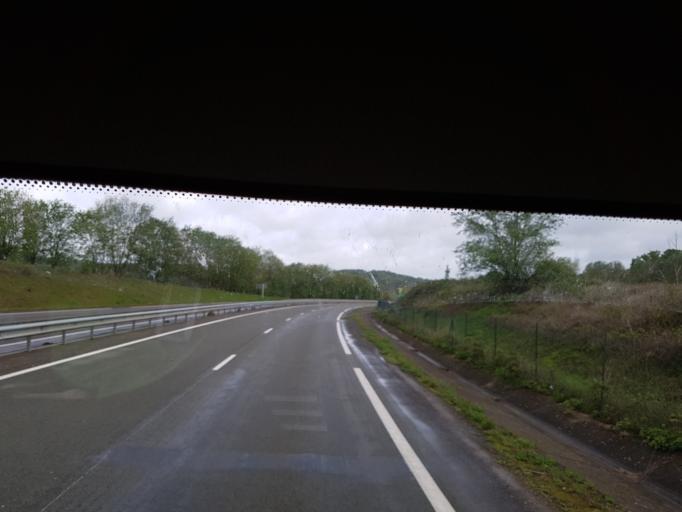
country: FR
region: Picardie
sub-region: Departement de l'Aisne
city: Courmelles
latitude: 49.3532
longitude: 3.3125
